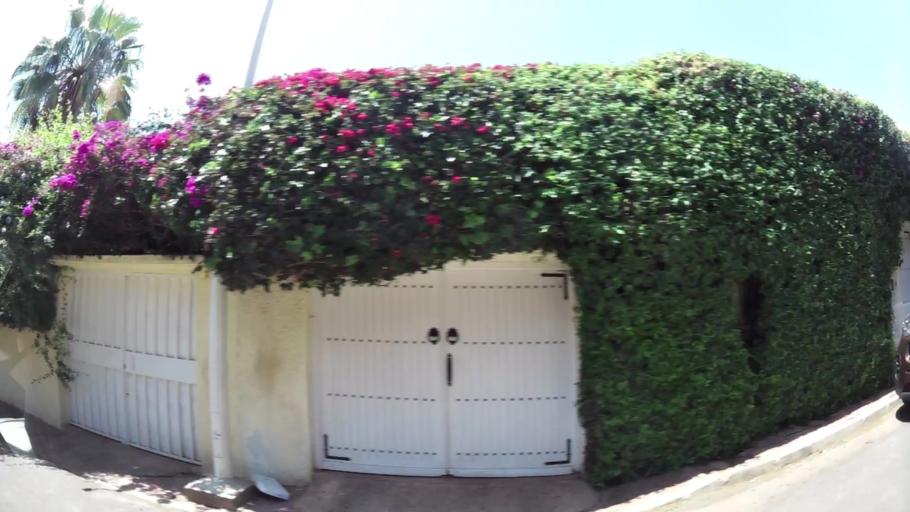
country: MA
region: Souss-Massa-Draa
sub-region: Agadir-Ida-ou-Tnan
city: Agadir
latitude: 30.4365
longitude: -9.5841
